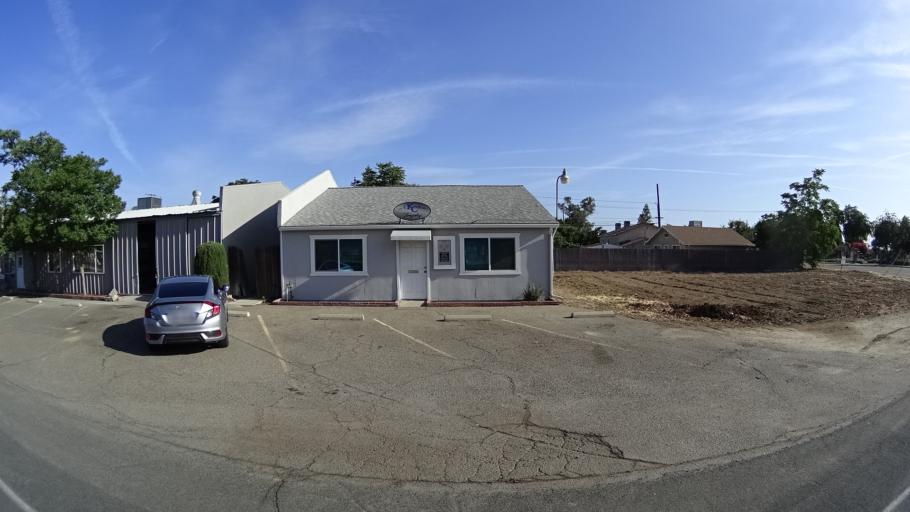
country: US
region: California
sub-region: Kings County
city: Hanford
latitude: 36.3225
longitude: -119.6375
